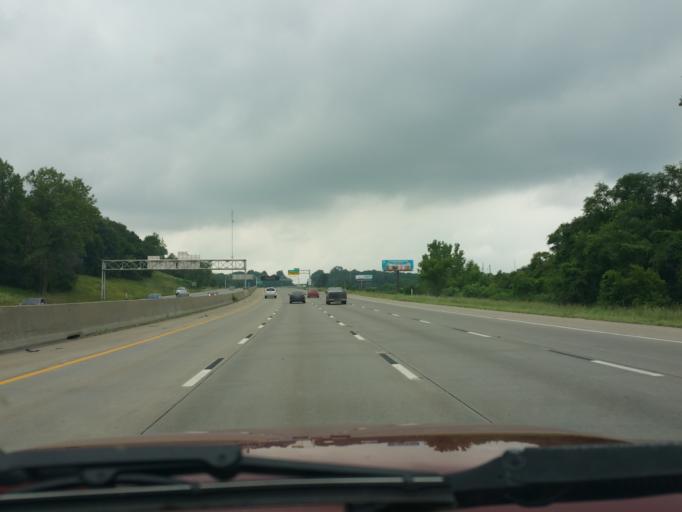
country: US
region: Kansas
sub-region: Johnson County
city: Shawnee
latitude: 39.0722
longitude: -94.6806
